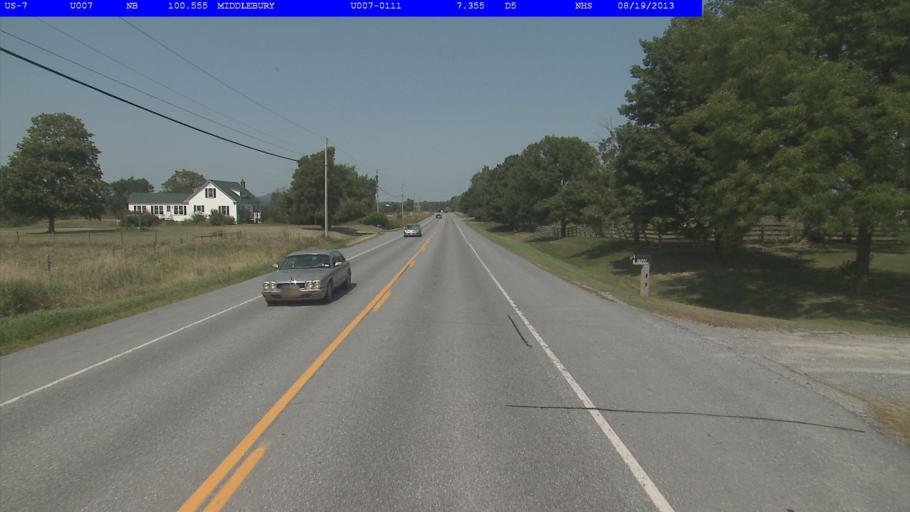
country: US
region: Vermont
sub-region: Addison County
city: Middlebury (village)
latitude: 44.0452
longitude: -73.1629
